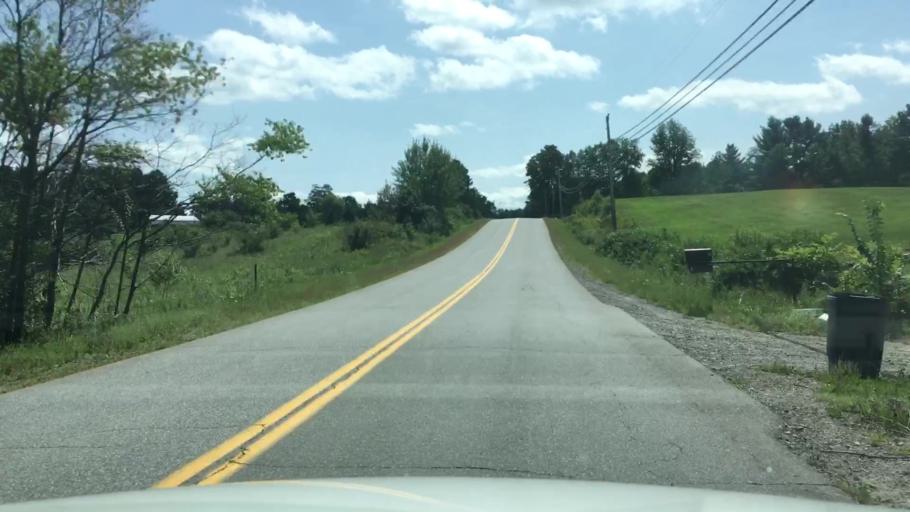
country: US
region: Maine
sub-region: Kennebec County
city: Augusta
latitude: 44.3485
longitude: -69.8115
